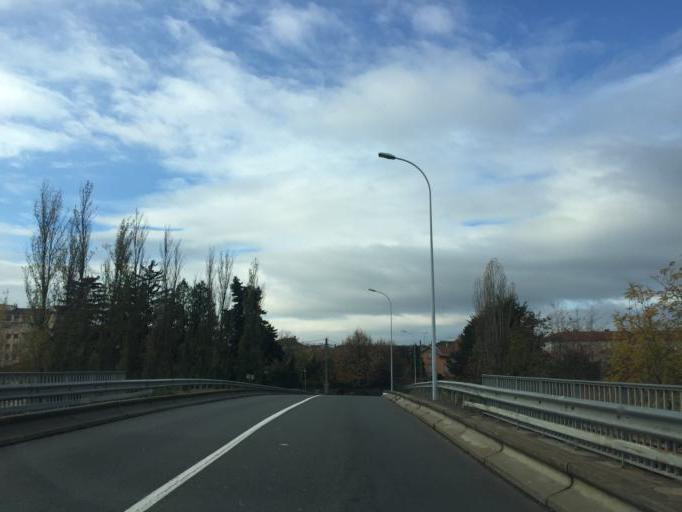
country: FR
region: Rhone-Alpes
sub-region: Departement du Rhone
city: Villefranche-sur-Saone
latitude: 45.9956
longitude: 4.7231
